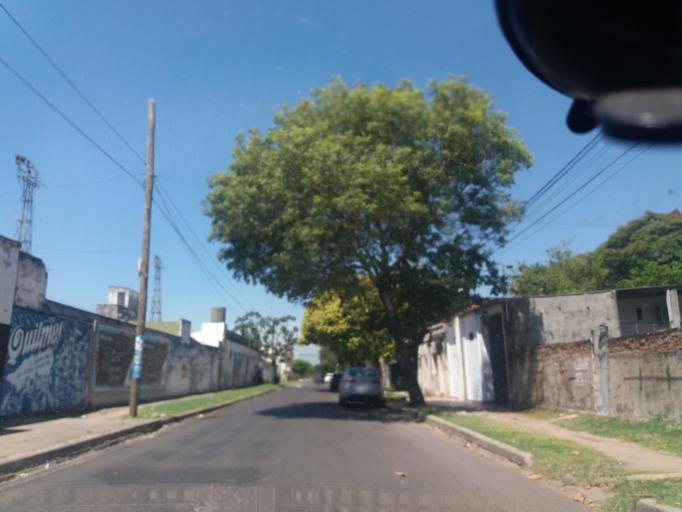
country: AR
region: Corrientes
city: Corrientes
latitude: -27.4821
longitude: -58.8453
